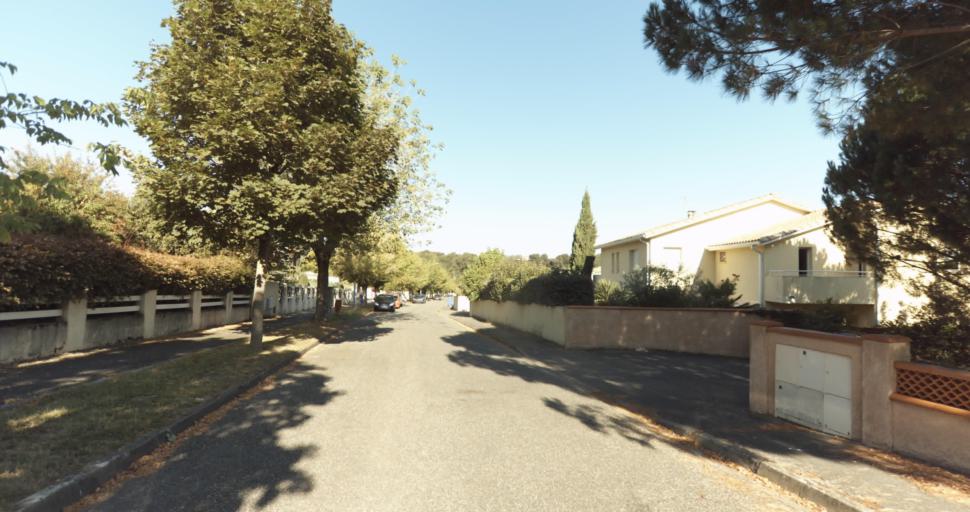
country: FR
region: Midi-Pyrenees
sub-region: Departement de la Haute-Garonne
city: L'Union
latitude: 43.6681
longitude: 1.4806
